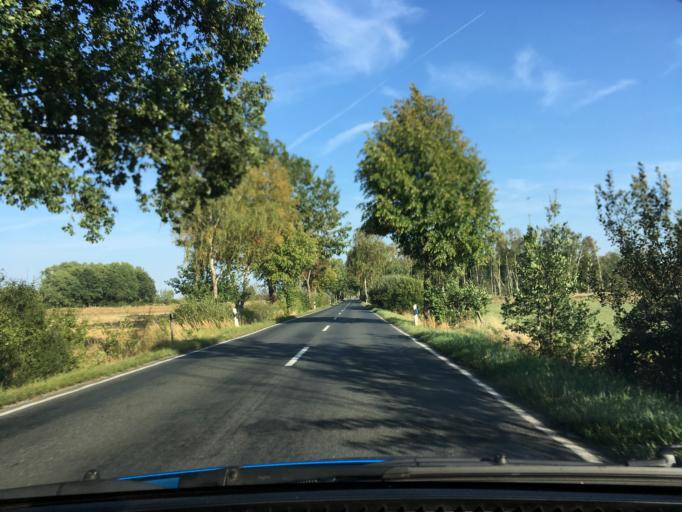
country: DE
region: Lower Saxony
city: Burgdorf
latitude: 52.4753
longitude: 9.9536
